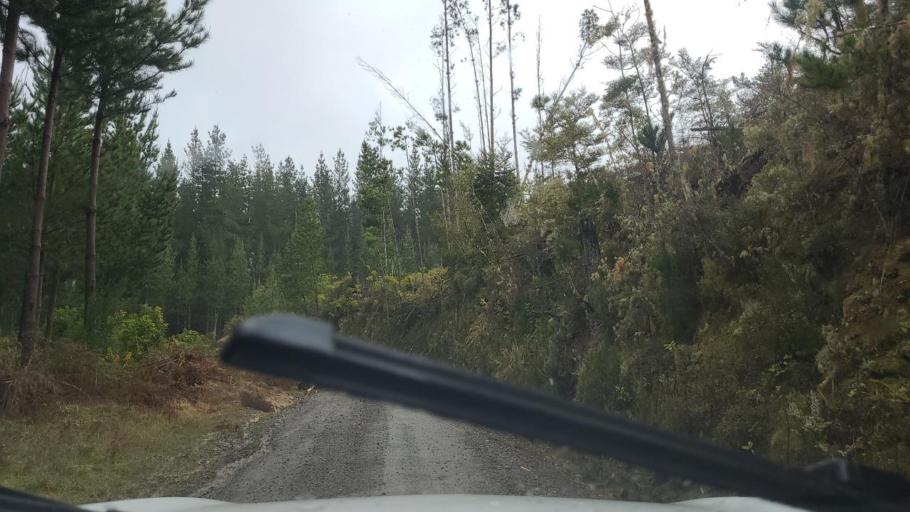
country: NZ
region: Wellington
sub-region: Masterton District
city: Masterton
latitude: -41.1737
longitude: 175.8667
